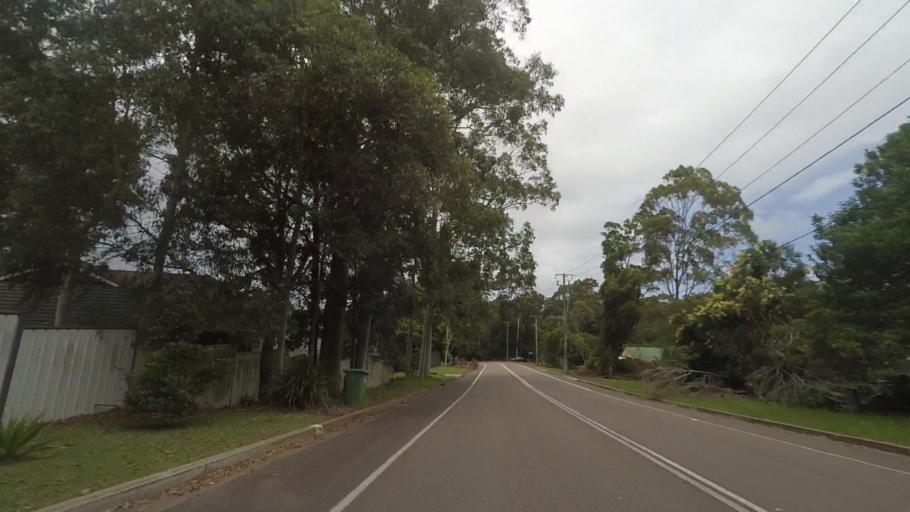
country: AU
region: New South Wales
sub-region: Wyong Shire
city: Chittaway Bay
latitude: -33.3405
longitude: 151.4200
